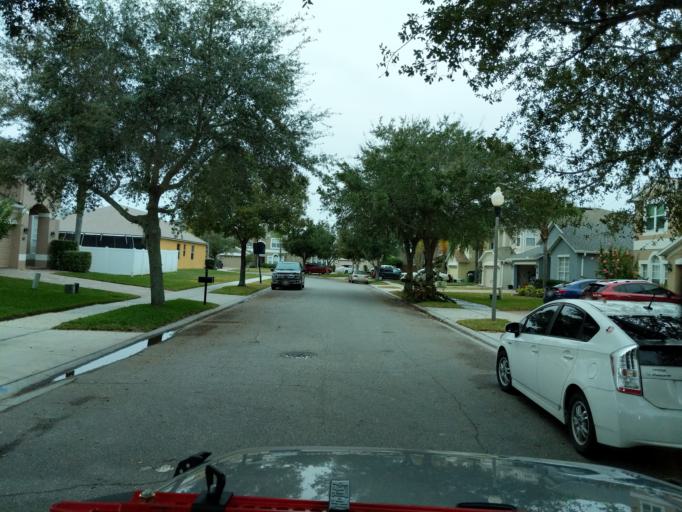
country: US
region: Florida
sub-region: Orange County
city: Winter Garden
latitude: 28.5269
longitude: -81.5836
